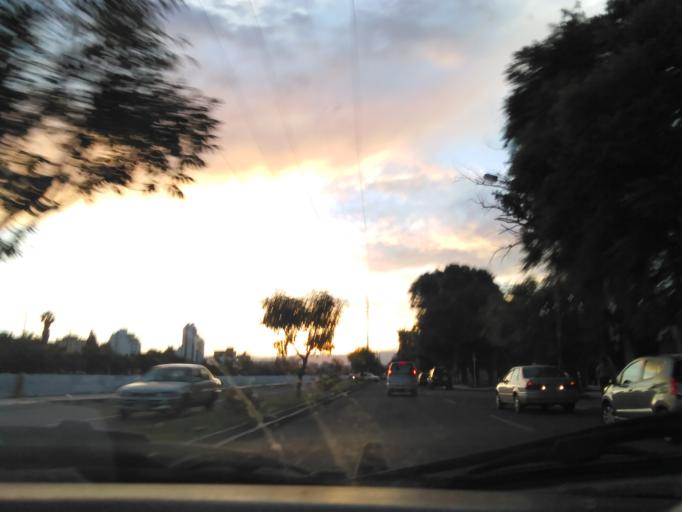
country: BO
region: Cochabamba
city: Cochabamba
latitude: -17.3776
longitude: -66.1459
